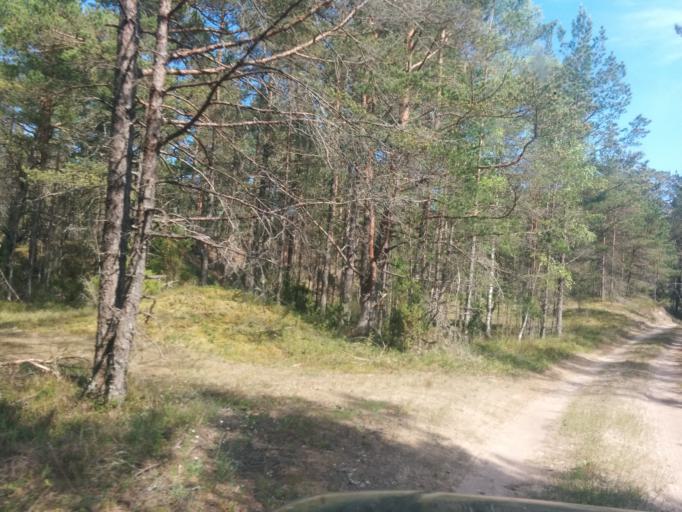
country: LV
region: Dundaga
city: Dundaga
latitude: 57.6216
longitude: 22.0806
